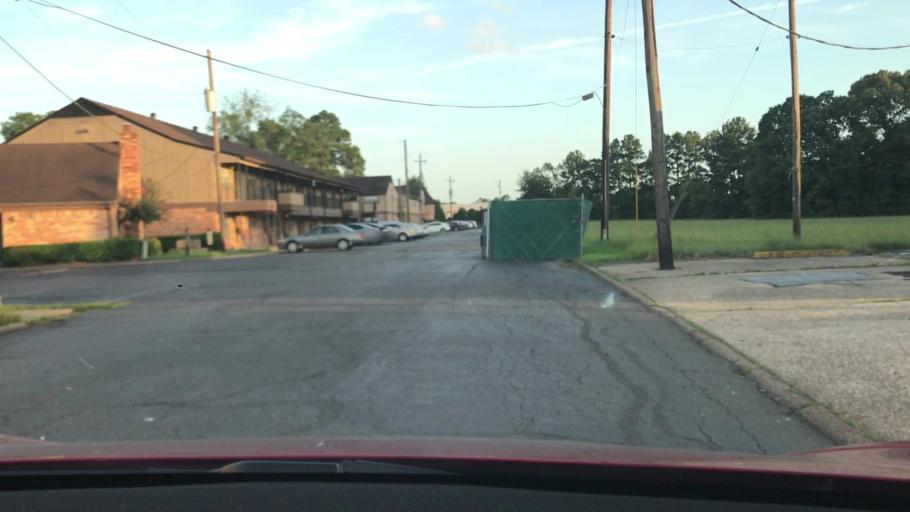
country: US
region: Louisiana
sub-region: De Soto Parish
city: Stonewall
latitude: 32.4018
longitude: -93.7914
